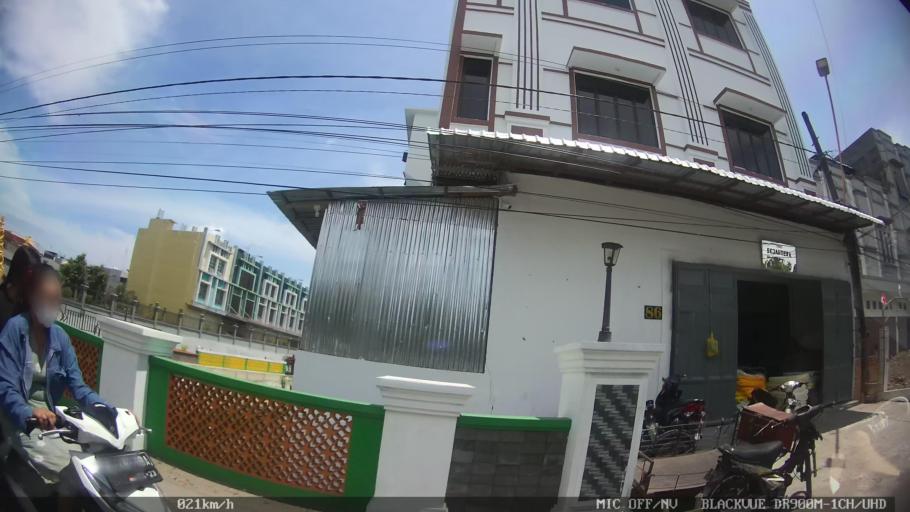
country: ID
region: North Sumatra
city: Binjai
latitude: 3.6000
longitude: 98.4873
